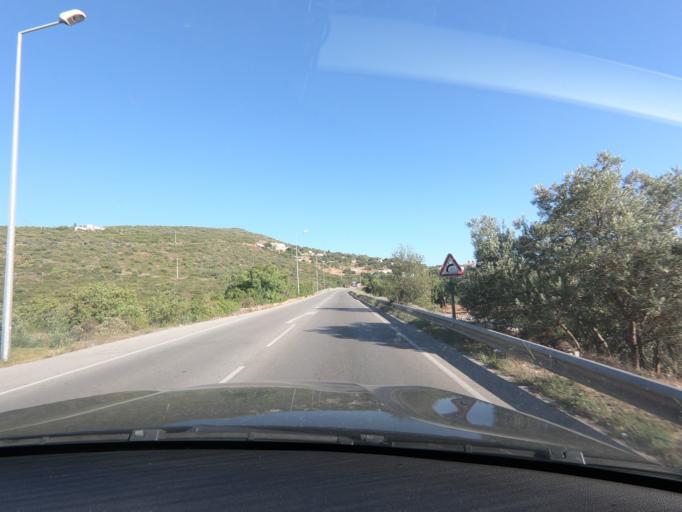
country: PT
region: Faro
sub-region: Loule
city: Loule
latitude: 37.1169
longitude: -8.0097
